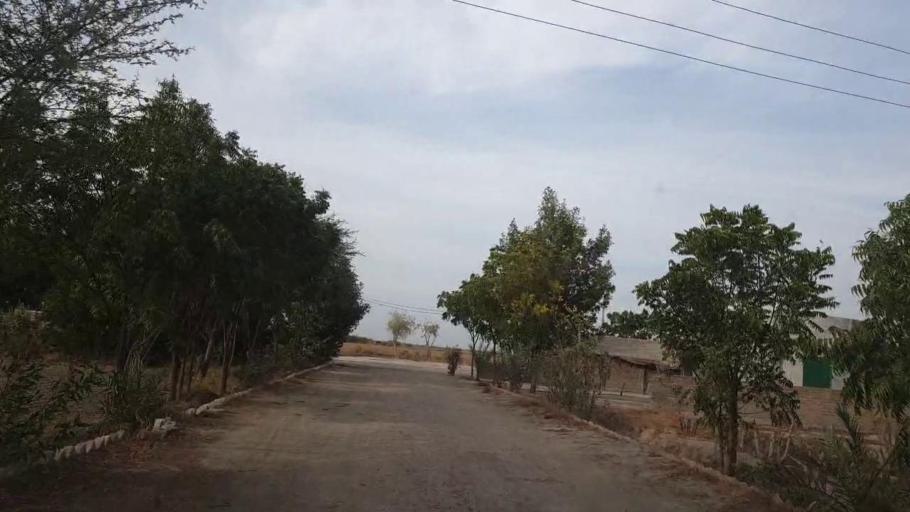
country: PK
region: Sindh
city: Nabisar
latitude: 25.0090
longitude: 69.5356
